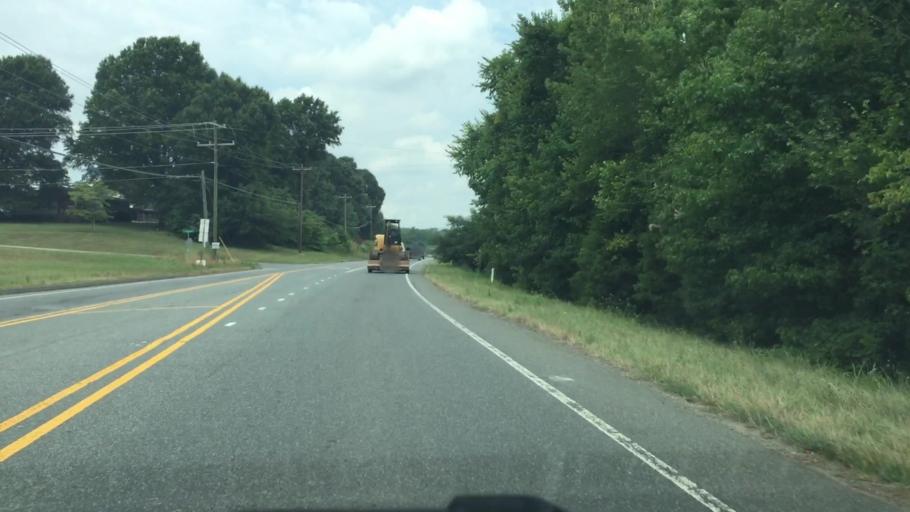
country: US
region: North Carolina
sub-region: Iredell County
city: Troutman
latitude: 35.6586
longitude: -80.8483
